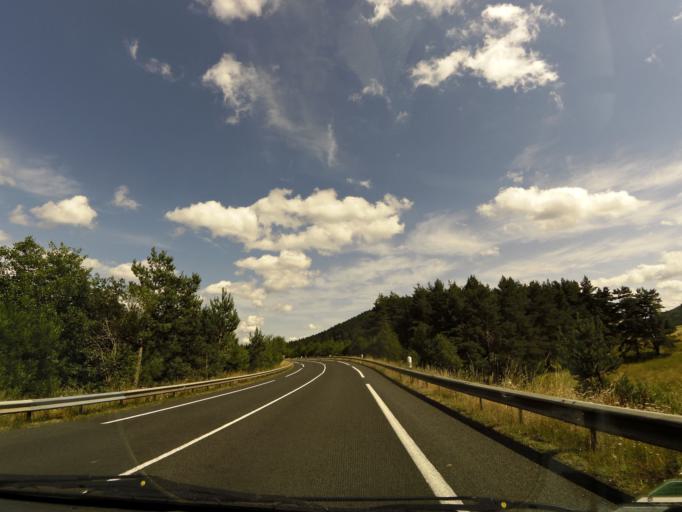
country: FR
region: Auvergne
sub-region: Departement du Puy-de-Dome
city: Aydat
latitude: 45.6840
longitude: 2.9479
